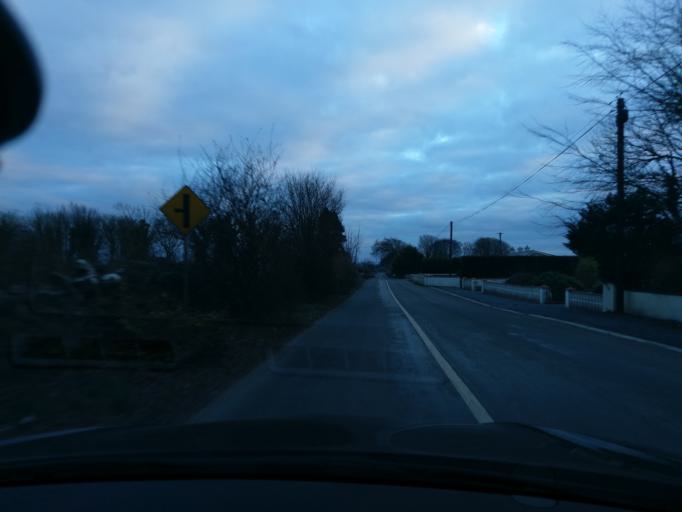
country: IE
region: Connaught
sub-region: County Galway
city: Athenry
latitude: 53.3306
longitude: -8.7676
